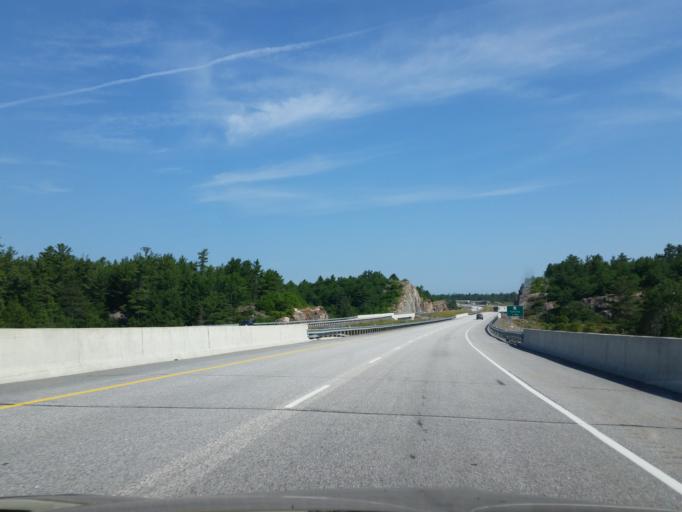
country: CA
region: Ontario
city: Greater Sudbury
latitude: 46.2131
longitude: -80.7692
